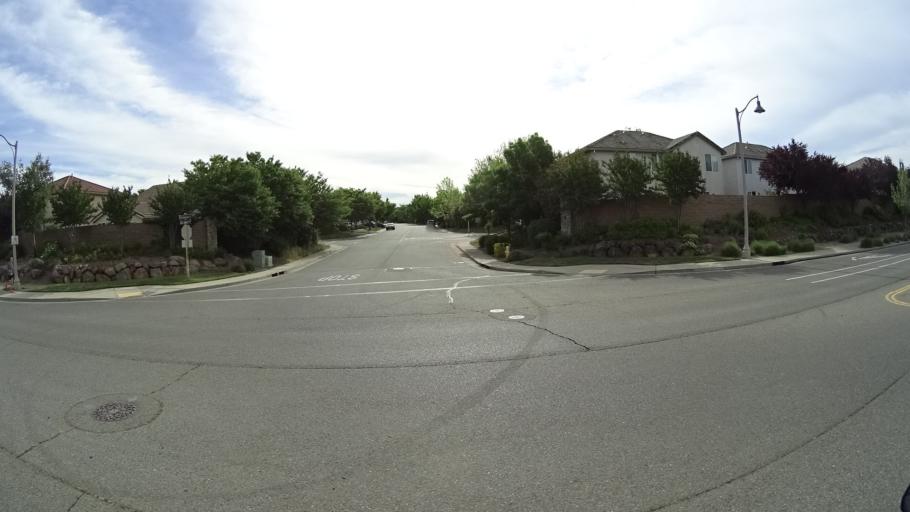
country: US
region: California
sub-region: Placer County
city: Lincoln
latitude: 38.8407
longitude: -121.2907
